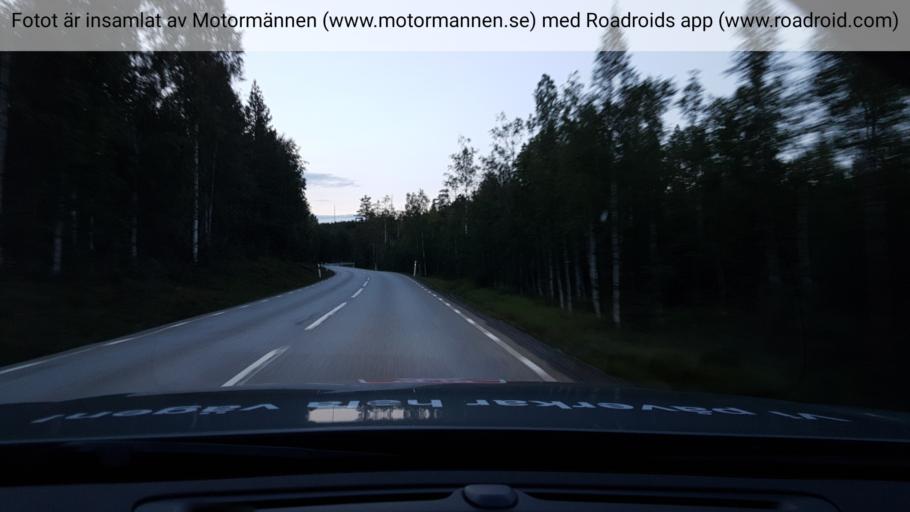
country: SE
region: OErebro
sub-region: Ljusnarsbergs Kommun
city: Kopparberg
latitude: 59.8382
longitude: 14.9974
